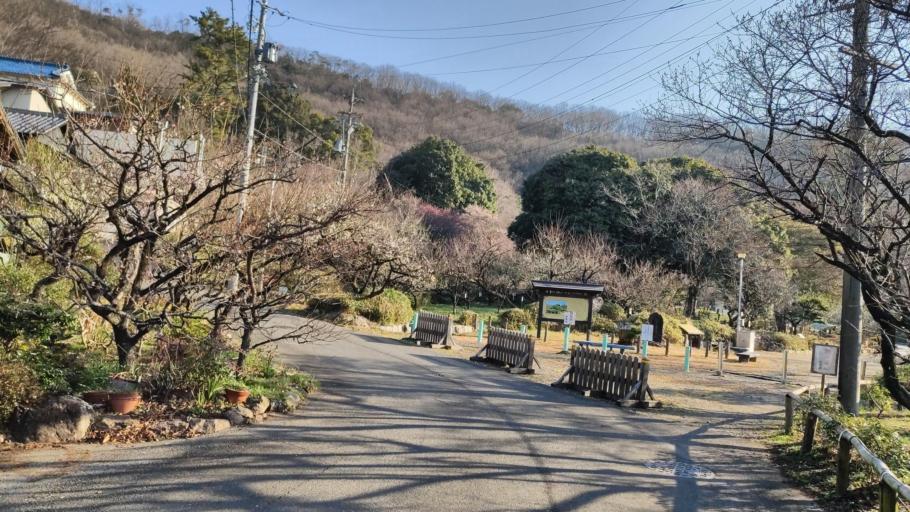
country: JP
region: Gifu
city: Gifu-shi
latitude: 35.4184
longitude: 136.7703
